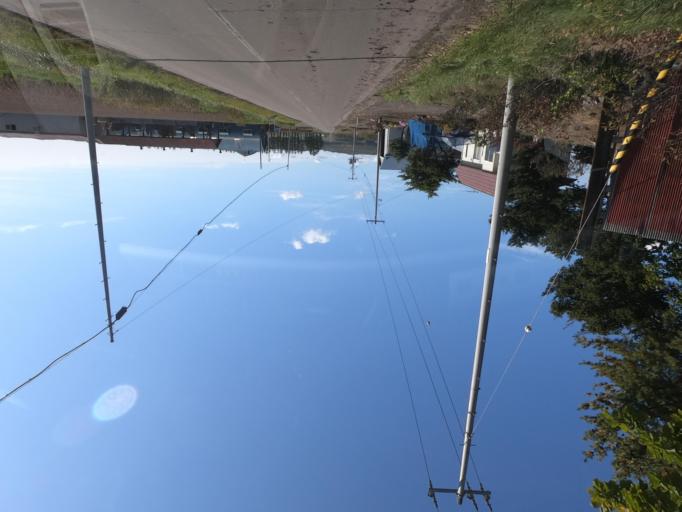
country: JP
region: Hokkaido
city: Otofuke
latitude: 43.0607
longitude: 143.2658
